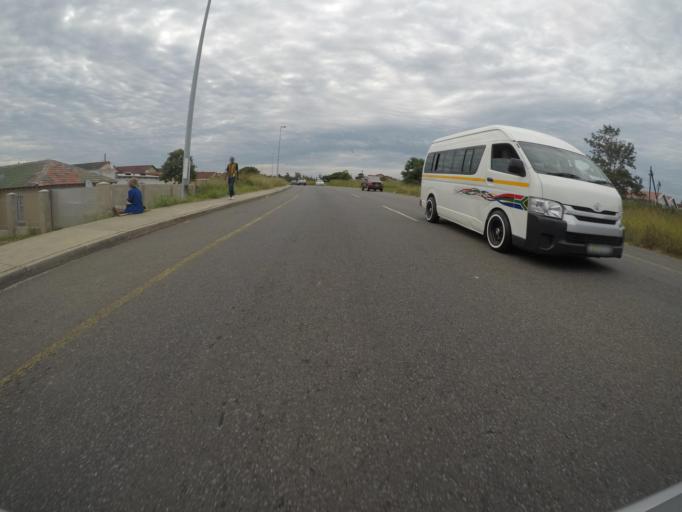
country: ZA
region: Eastern Cape
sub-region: Buffalo City Metropolitan Municipality
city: East London
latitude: -32.9787
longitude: 27.8585
